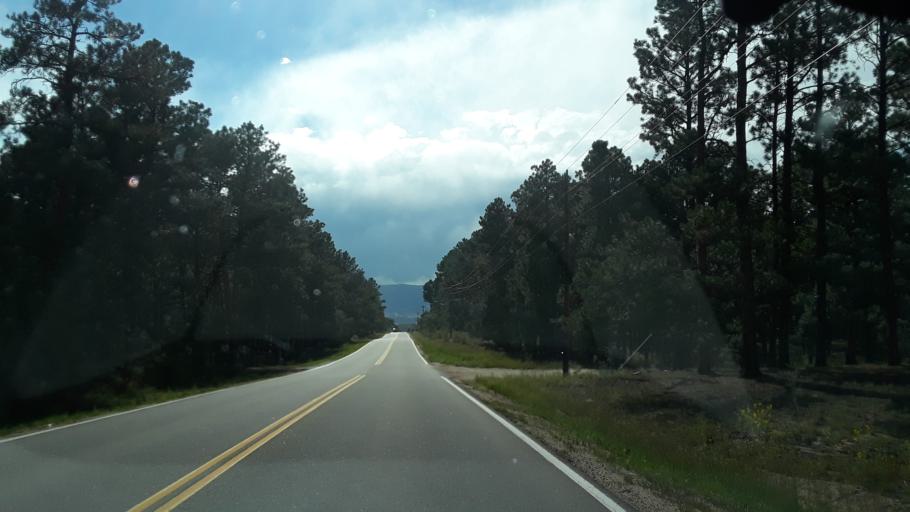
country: US
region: Colorado
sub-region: El Paso County
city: Black Forest
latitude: 39.0128
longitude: -104.7477
